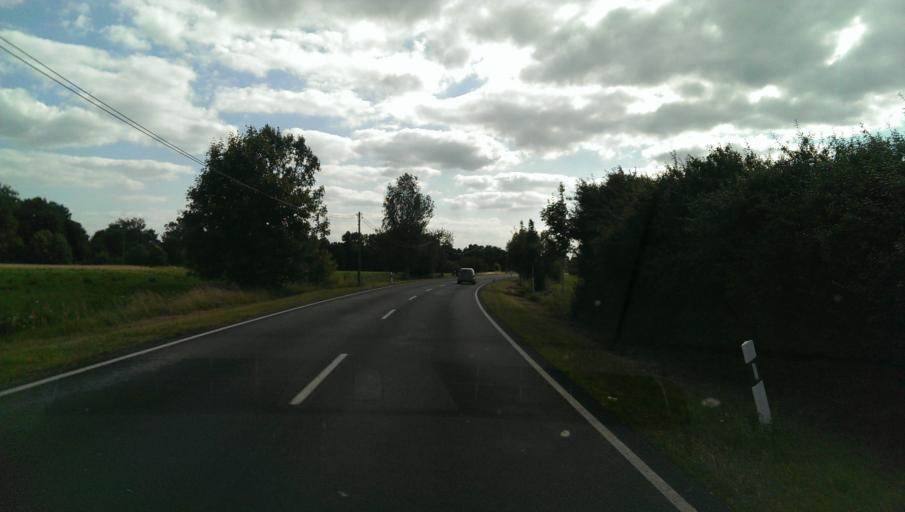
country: DE
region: Saxony-Anhalt
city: Grafenhainichen
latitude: 51.7331
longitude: 12.4765
